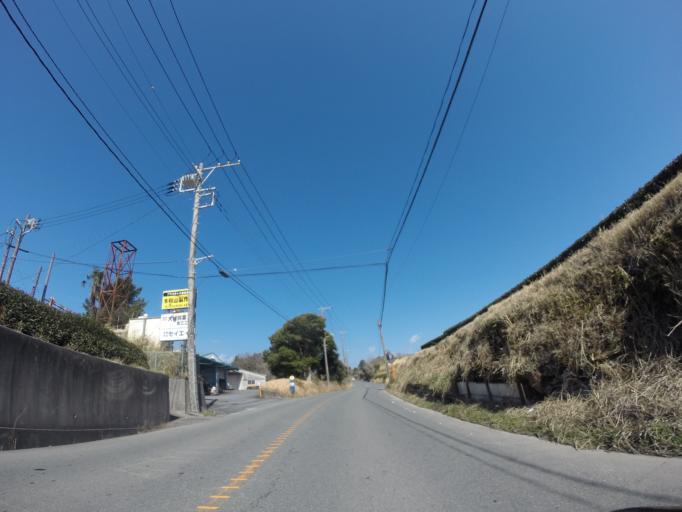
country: JP
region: Shizuoka
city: Numazu
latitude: 35.1370
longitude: 138.8361
